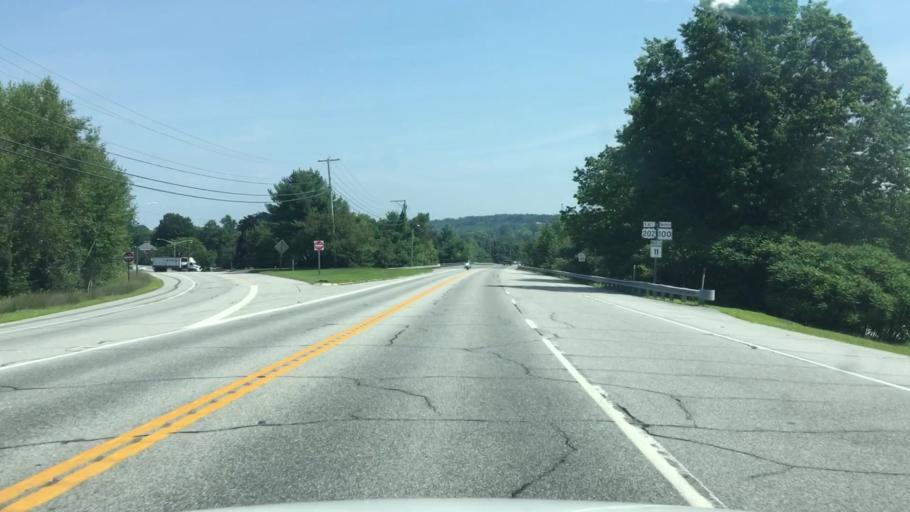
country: US
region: Maine
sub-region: Kennebec County
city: Winthrop
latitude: 44.2984
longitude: -69.9814
